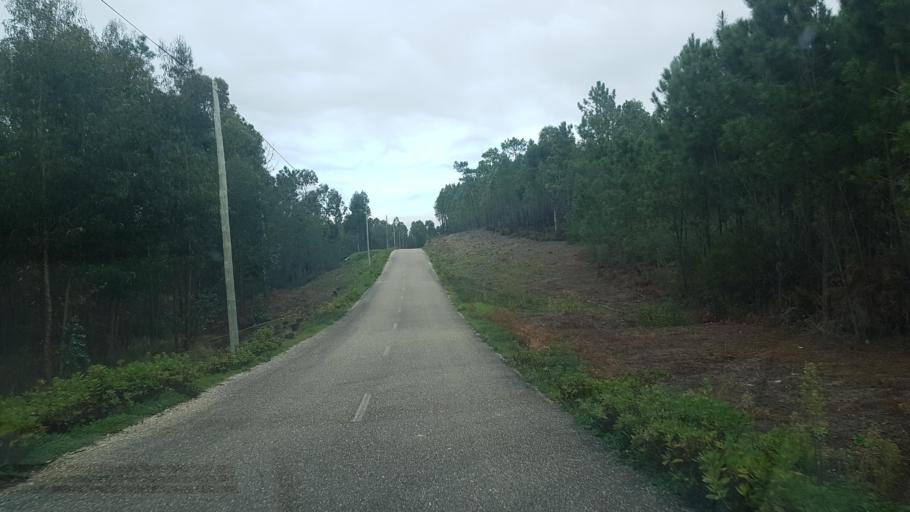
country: PT
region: Castelo Branco
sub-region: Vila de Rei
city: Vila de Rei
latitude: 39.5940
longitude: -8.1190
